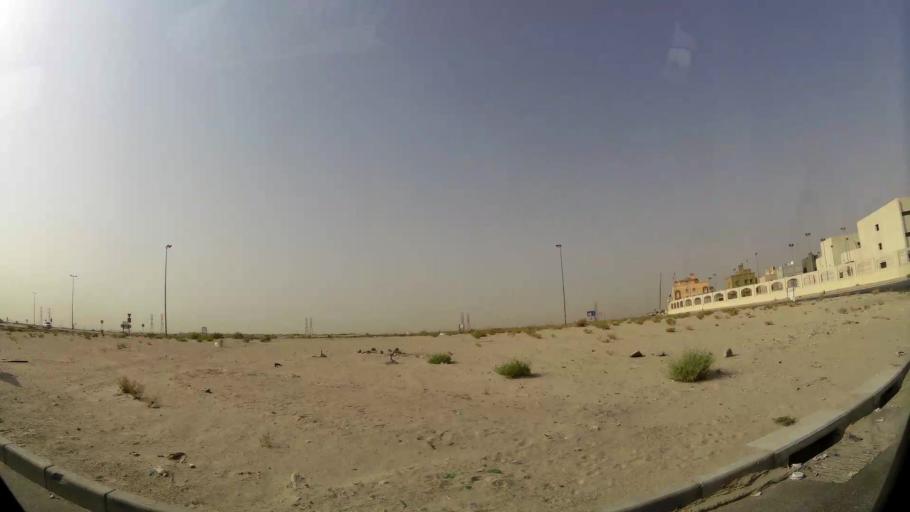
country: KW
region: Muhafazat al Jahra'
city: Al Jahra'
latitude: 29.3429
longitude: 47.7483
